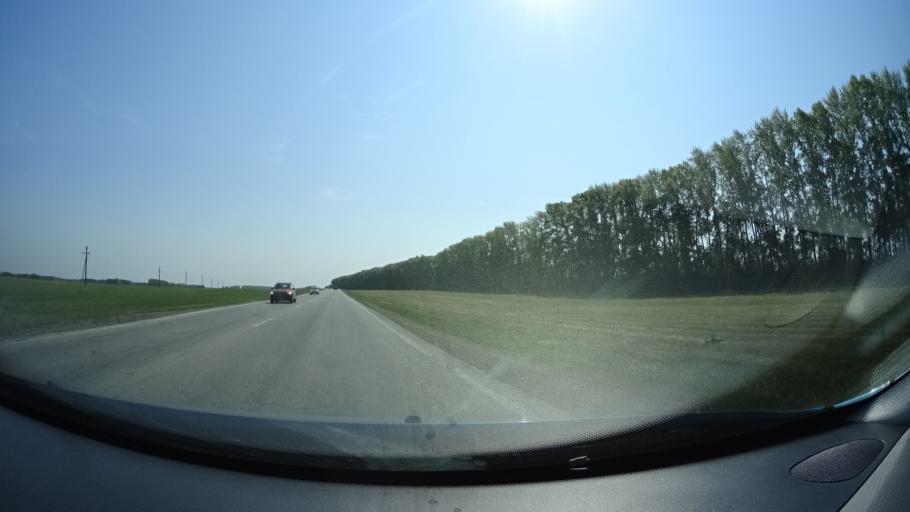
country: RU
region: Bashkortostan
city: Karmaskaly
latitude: 54.4058
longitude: 56.0783
